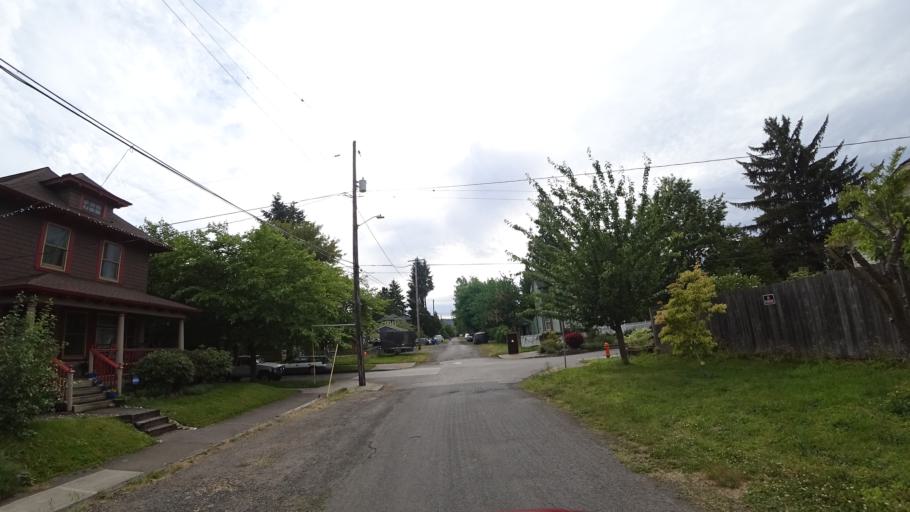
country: US
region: Oregon
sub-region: Multnomah County
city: Portland
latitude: 45.5758
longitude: -122.6979
